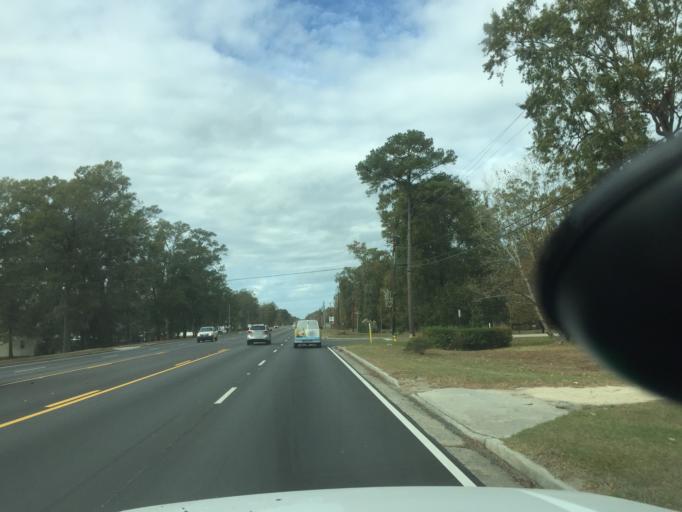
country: US
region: Georgia
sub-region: Chatham County
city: Garden City
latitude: 32.0891
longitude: -81.1802
